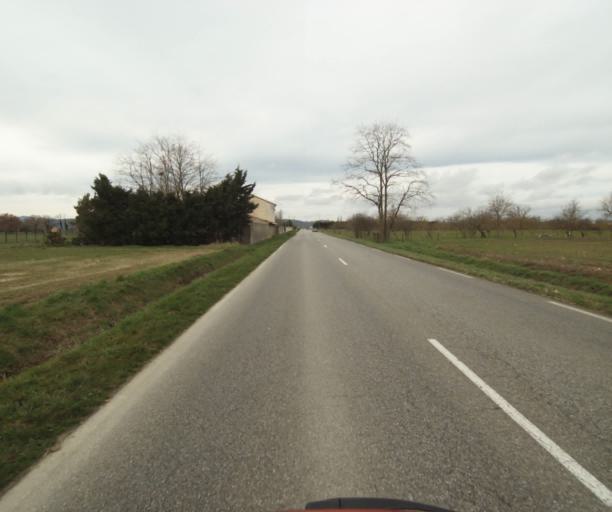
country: FR
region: Midi-Pyrenees
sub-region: Departement de l'Ariege
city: La Tour-du-Crieu
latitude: 43.0961
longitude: 1.6621
